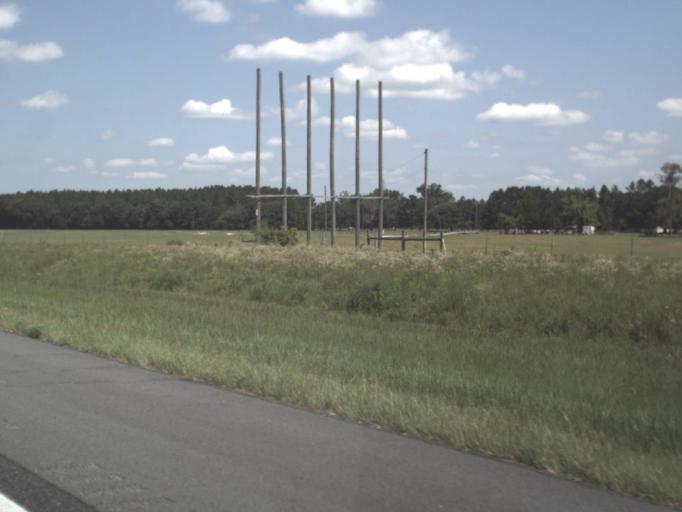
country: US
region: Florida
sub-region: Madison County
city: Madison
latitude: 30.3776
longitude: -83.2873
